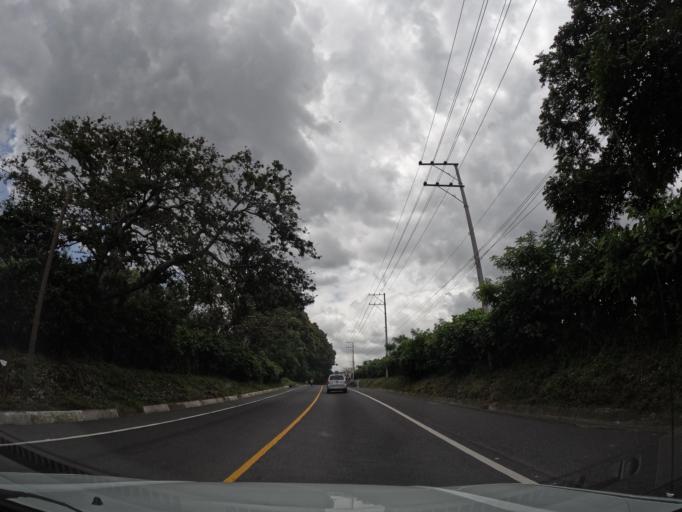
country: GT
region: Sacatepequez
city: San Miguel Duenas
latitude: 14.5025
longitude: -90.7936
